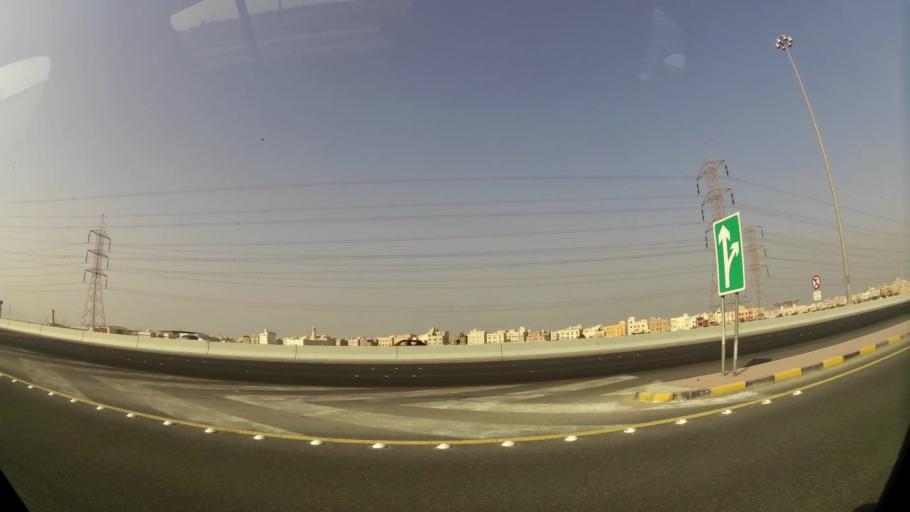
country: KW
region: Al Asimah
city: Ar Rabiyah
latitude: 29.2954
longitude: 47.7956
